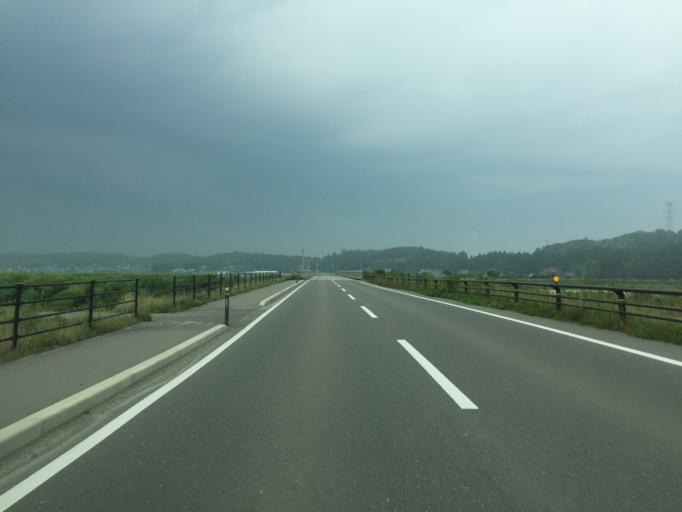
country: JP
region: Fukushima
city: Namie
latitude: 37.6410
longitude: 141.0162
